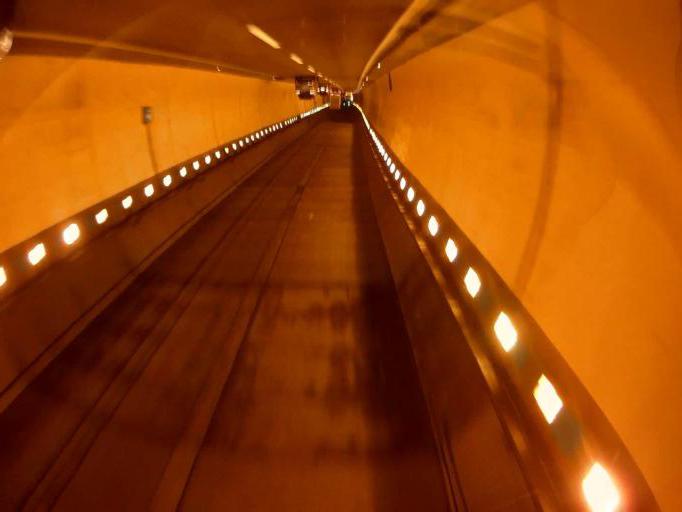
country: IT
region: Trentino-Alto Adige
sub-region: Bolzano
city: Cornaiano
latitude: 46.4832
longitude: 11.2968
